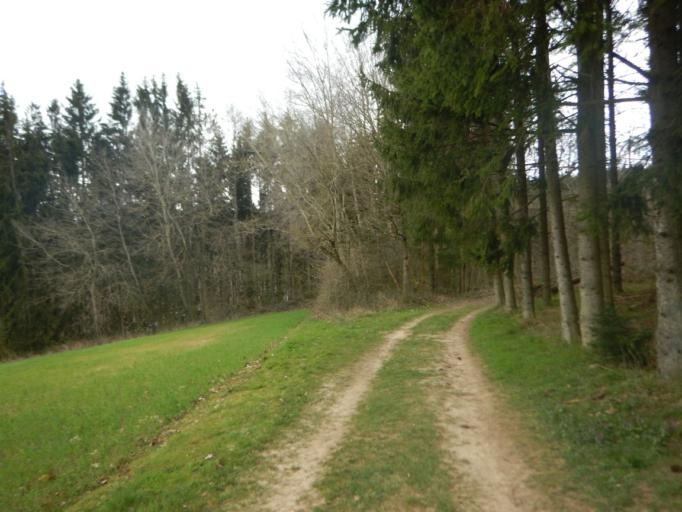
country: LU
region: Luxembourg
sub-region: Canton de Mersch
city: Lorentzweiler
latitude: 49.7059
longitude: 6.1550
